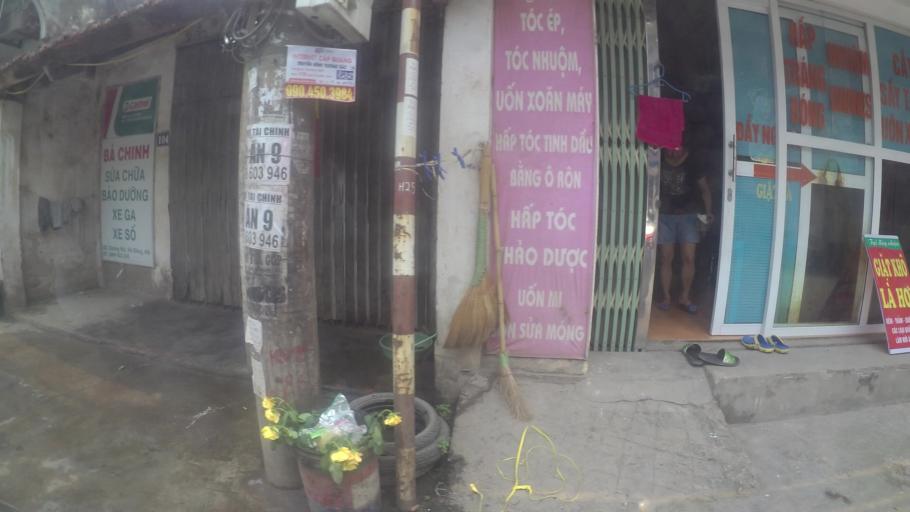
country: VN
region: Ha Noi
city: Ha Dong
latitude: 20.9810
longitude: 105.7487
